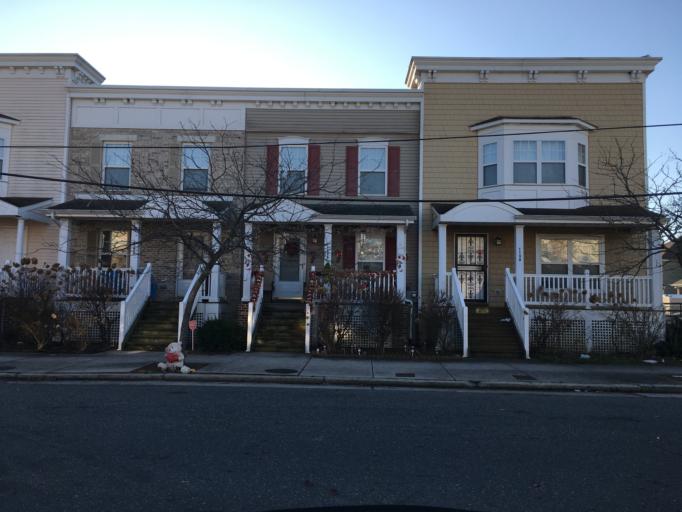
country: US
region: New Jersey
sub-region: Atlantic County
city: Atlantic City
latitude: 39.3683
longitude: -74.4282
